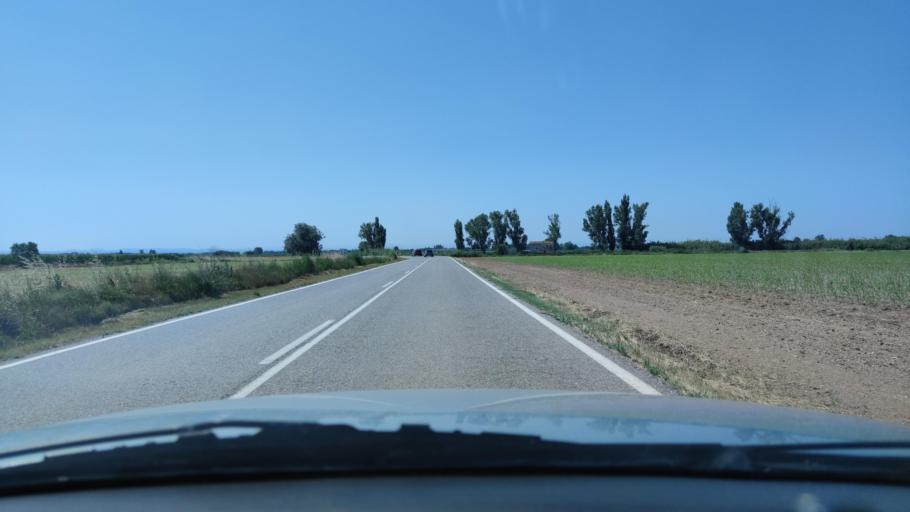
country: ES
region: Catalonia
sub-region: Provincia de Lleida
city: Ivars d'Urgell
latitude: 41.7122
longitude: 0.9823
